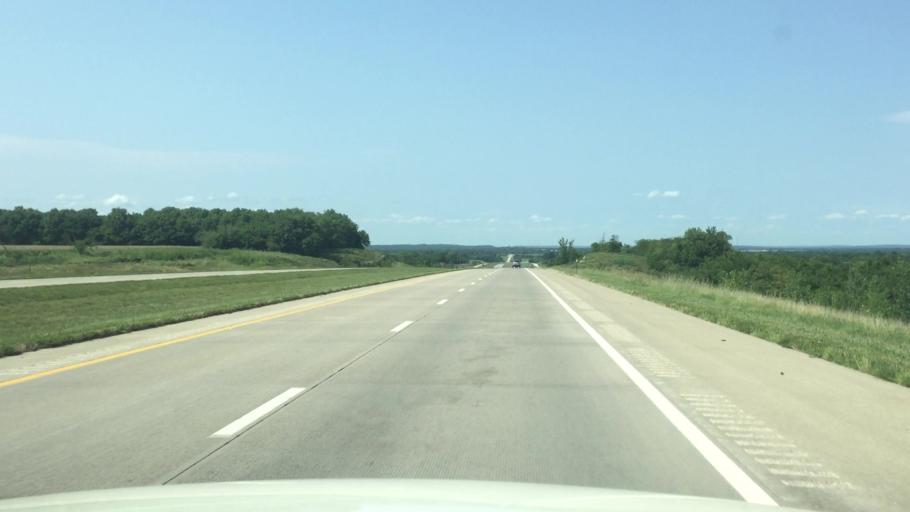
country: US
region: Kansas
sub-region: Linn County
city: Pleasanton
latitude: 38.1121
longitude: -94.7133
